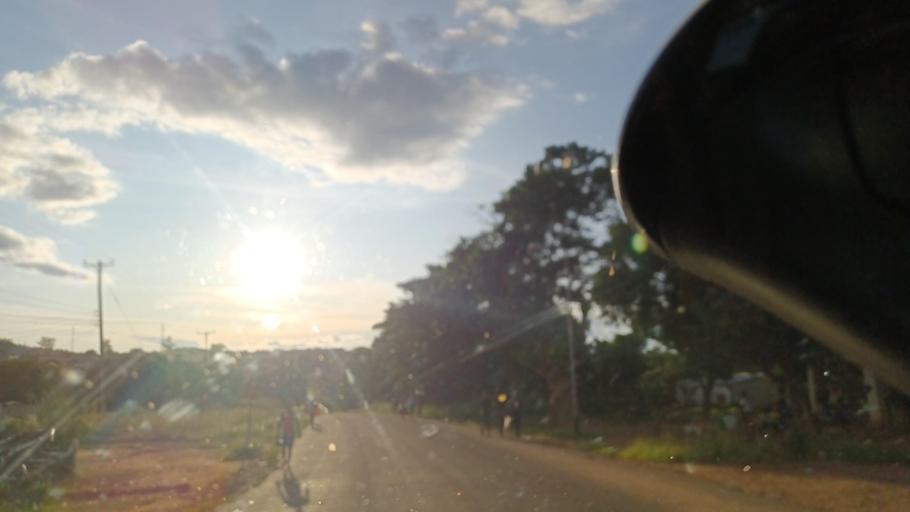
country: ZM
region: North-Western
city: Kasempa
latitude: -13.4586
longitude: 25.8474
